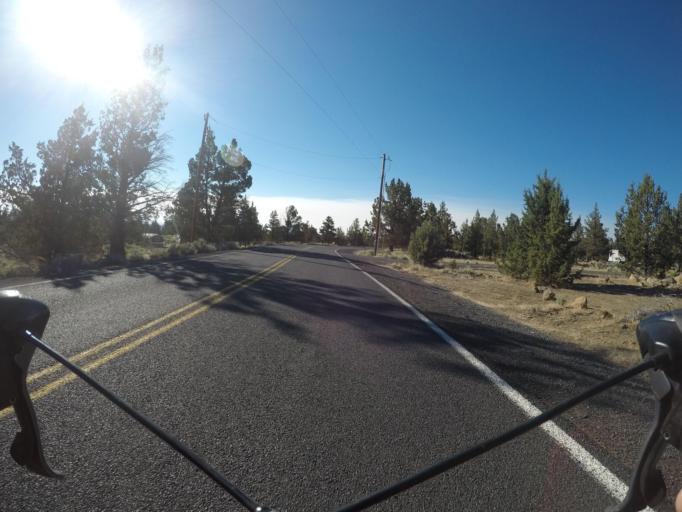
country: US
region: Oregon
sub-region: Deschutes County
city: Bend
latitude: 44.1763
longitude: -121.2658
